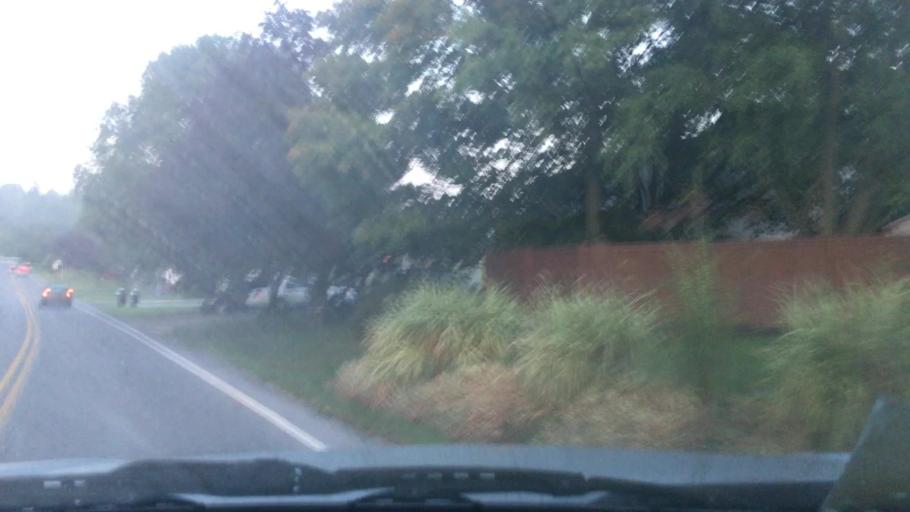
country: US
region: Pennsylvania
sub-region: Blair County
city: Duncansville
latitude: 40.4173
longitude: -78.4144
